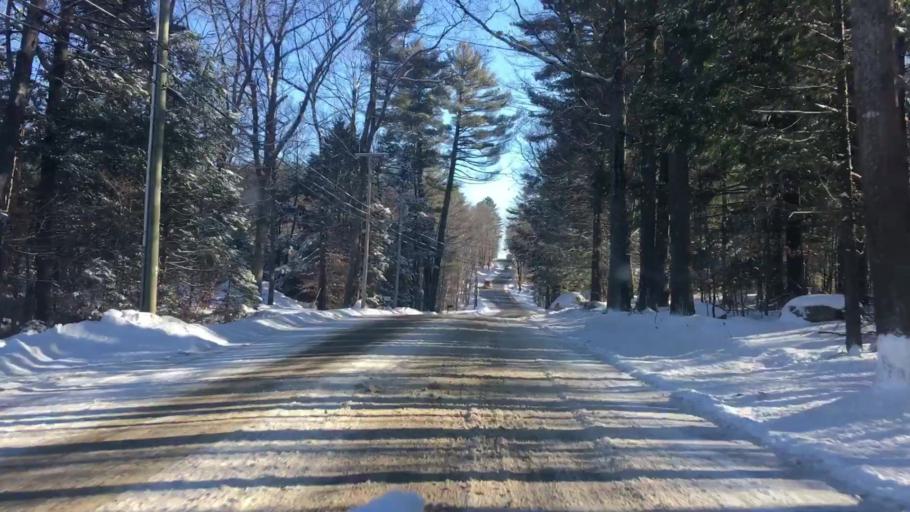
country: US
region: Maine
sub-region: Cumberland County
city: New Gloucester
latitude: 43.9505
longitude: -70.3062
